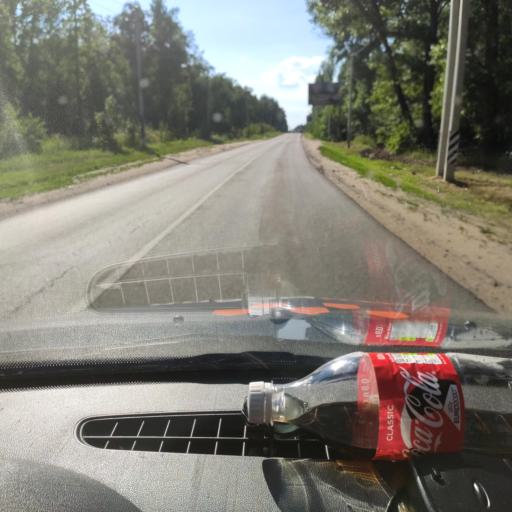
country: RU
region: Voronezj
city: Podgornoye
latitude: 51.7851
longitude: 39.1792
